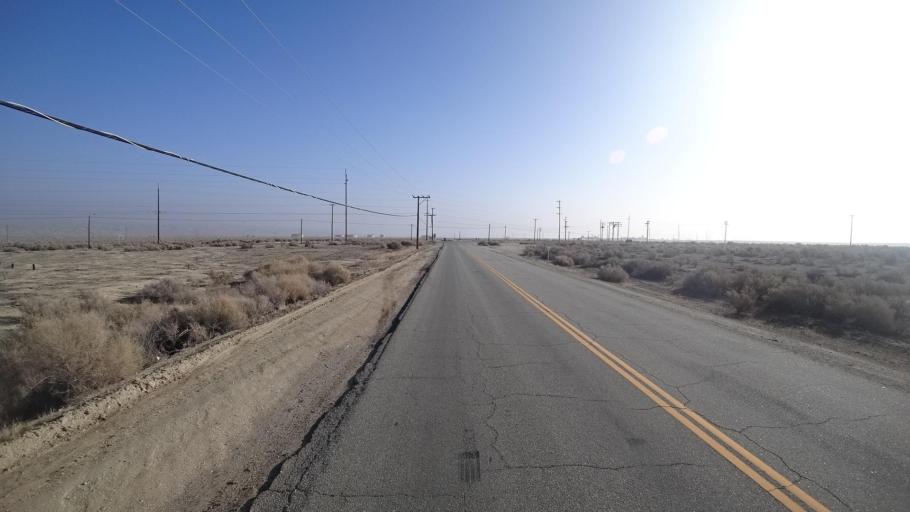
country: US
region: California
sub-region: Kern County
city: Taft Heights
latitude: 35.1801
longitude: -119.5292
